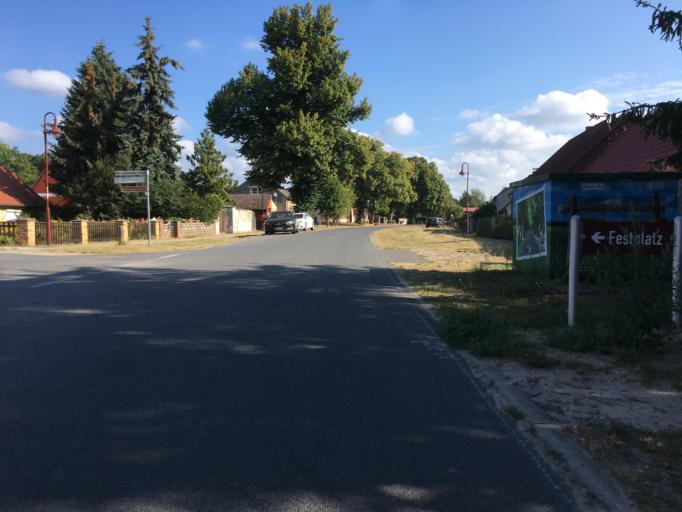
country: DE
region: Brandenburg
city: Liebenwalde
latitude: 52.9128
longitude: 13.4615
